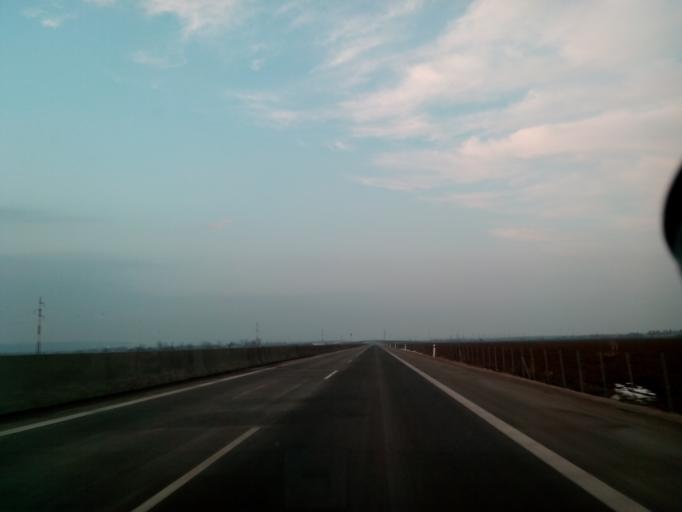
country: SK
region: Kosicky
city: Kosice
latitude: 48.5988
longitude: 21.2450
